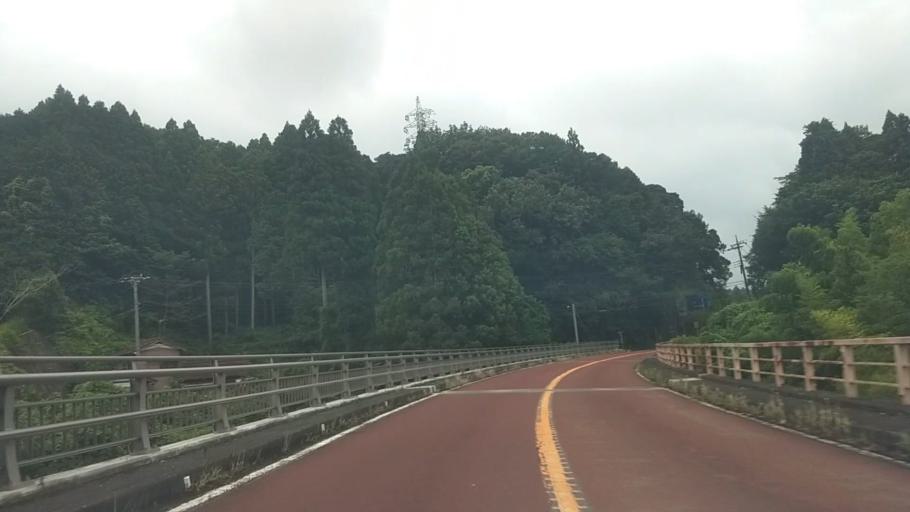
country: JP
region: Chiba
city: Kawaguchi
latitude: 35.2493
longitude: 140.0766
